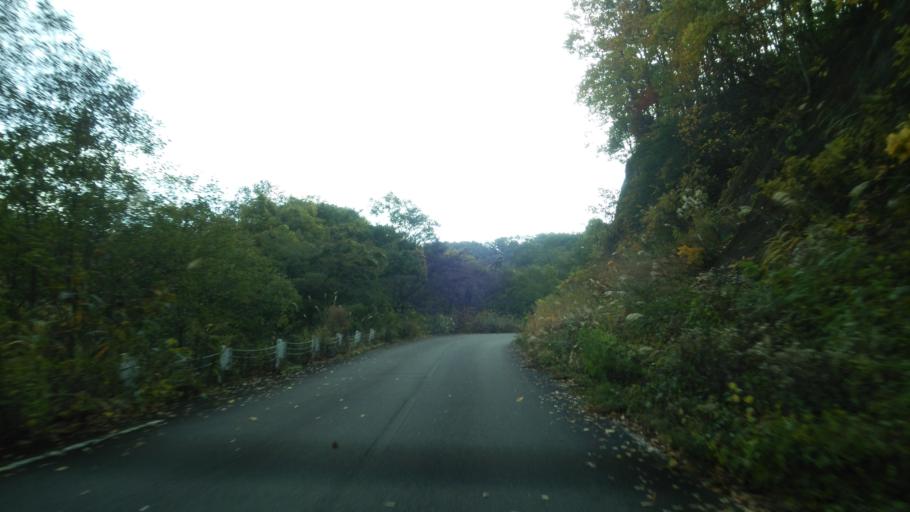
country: JP
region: Fukushima
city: Kitakata
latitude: 37.3990
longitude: 139.7425
